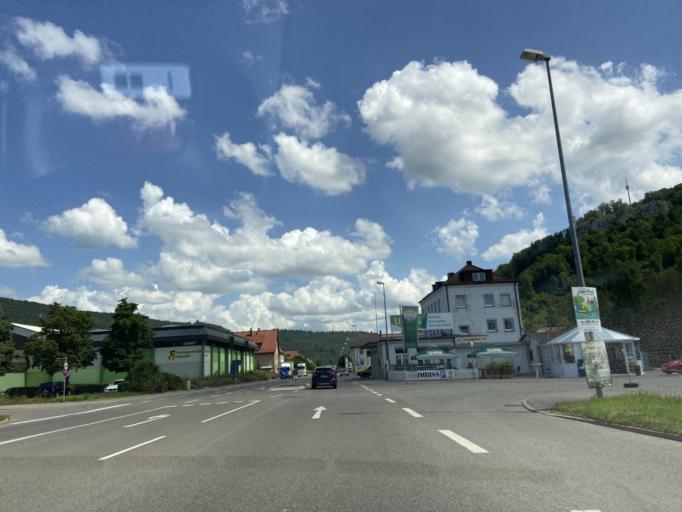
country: DE
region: Baden-Wuerttemberg
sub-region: Tuebingen Region
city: Albstadt
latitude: 48.2074
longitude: 9.0303
